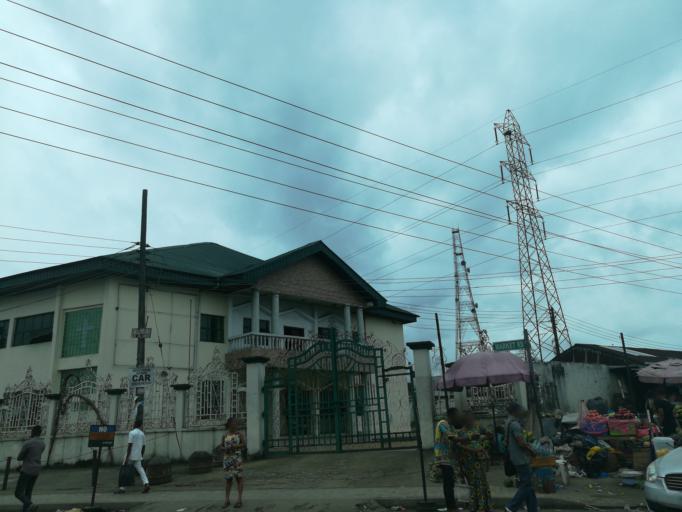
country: NG
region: Rivers
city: Port Harcourt
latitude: 4.8277
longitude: 7.0249
